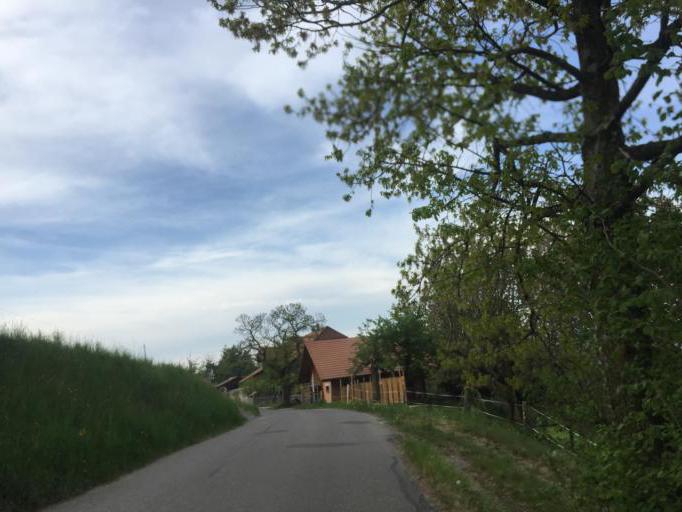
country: CH
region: Bern
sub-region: Bern-Mittelland District
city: Munsingen
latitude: 46.8570
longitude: 7.5474
